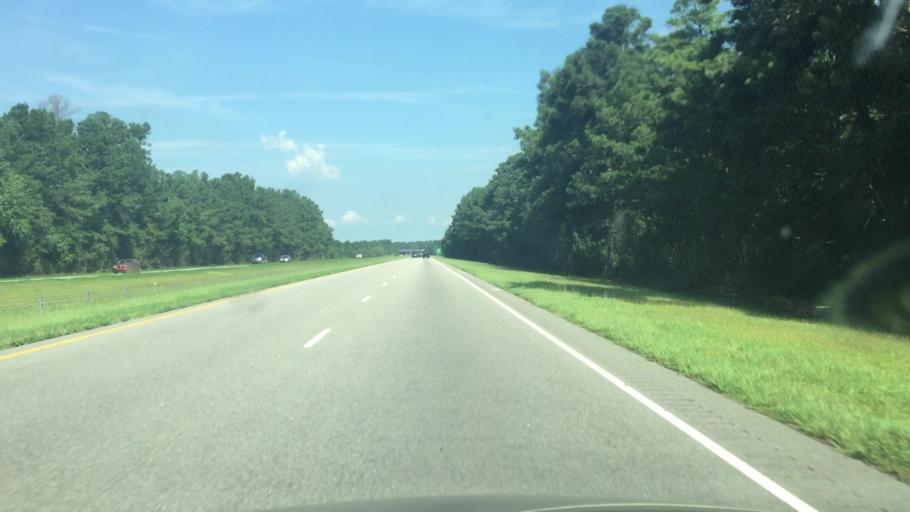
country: US
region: North Carolina
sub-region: Robeson County
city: Maxton
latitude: 34.7347
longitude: -79.3240
